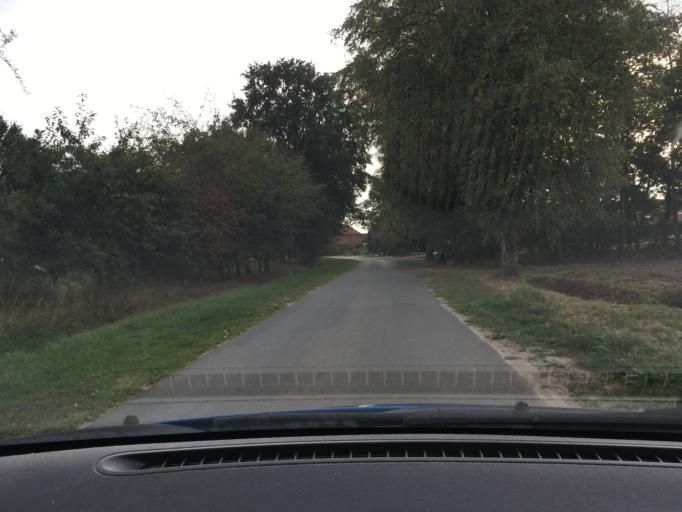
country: DE
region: Lower Saxony
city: Wietzendorf
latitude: 52.8984
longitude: 9.9553
